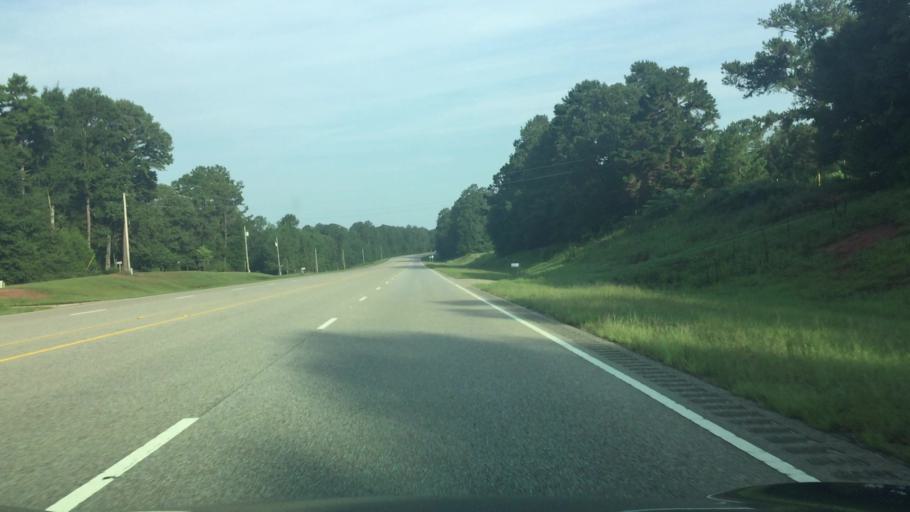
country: US
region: Alabama
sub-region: Covington County
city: Andalusia
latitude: 31.4039
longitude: -86.5938
